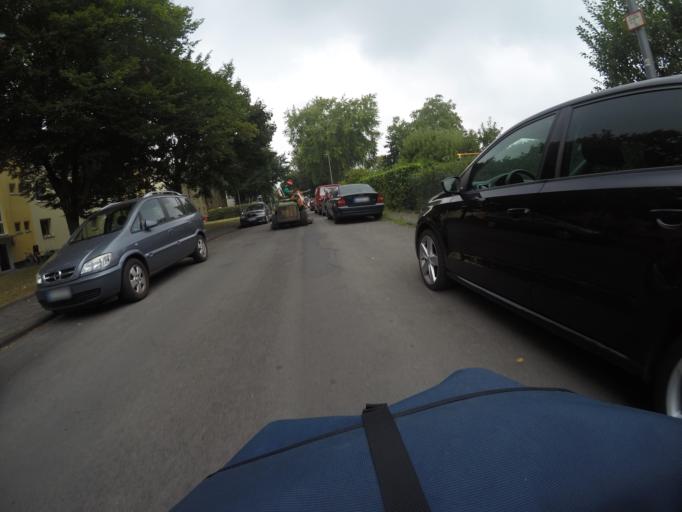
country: DE
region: North Rhine-Westphalia
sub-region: Regierungsbezirk Dusseldorf
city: Krefeld
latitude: 51.3239
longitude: 6.5809
